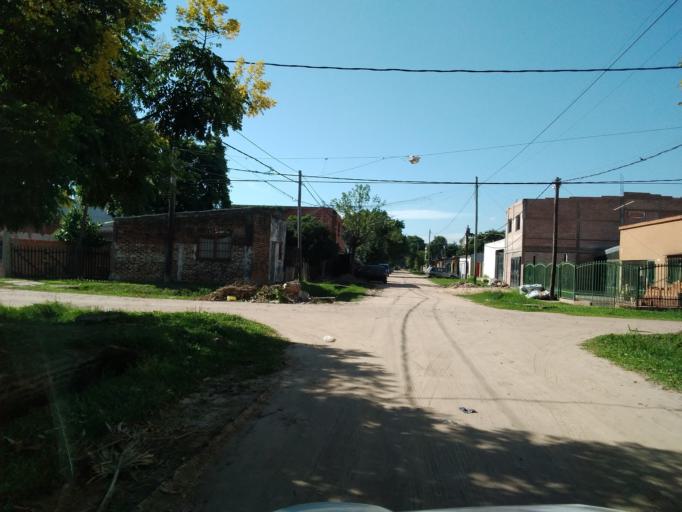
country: AR
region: Corrientes
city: Corrientes
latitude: -27.4848
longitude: -58.8048
